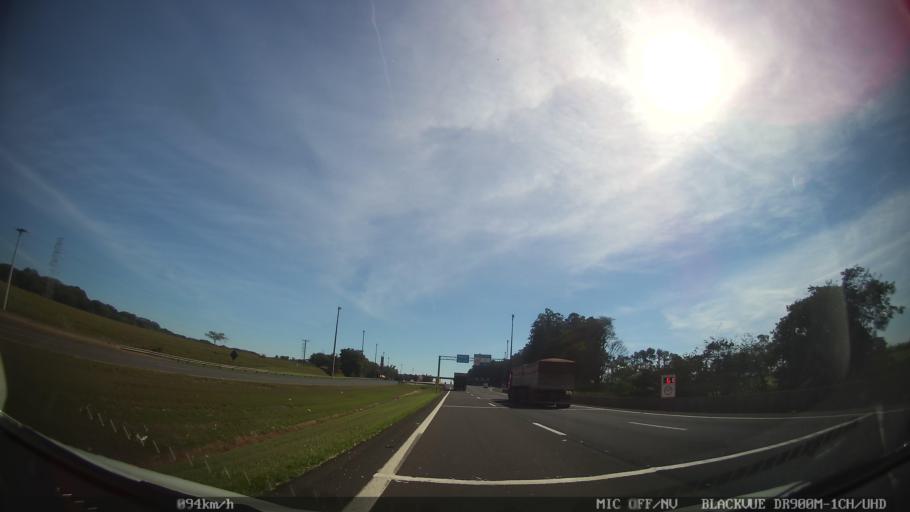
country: BR
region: Sao Paulo
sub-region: Pirassununga
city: Pirassununga
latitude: -21.9614
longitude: -47.4583
